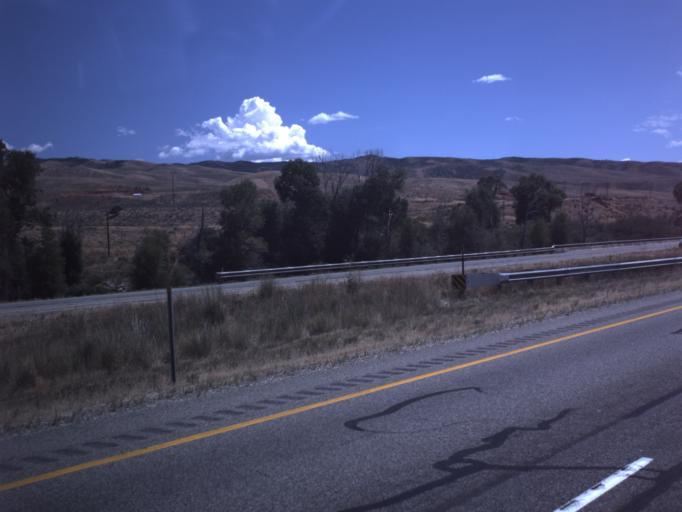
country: US
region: Utah
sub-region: Summit County
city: Coalville
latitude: 41.0363
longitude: -111.5110
